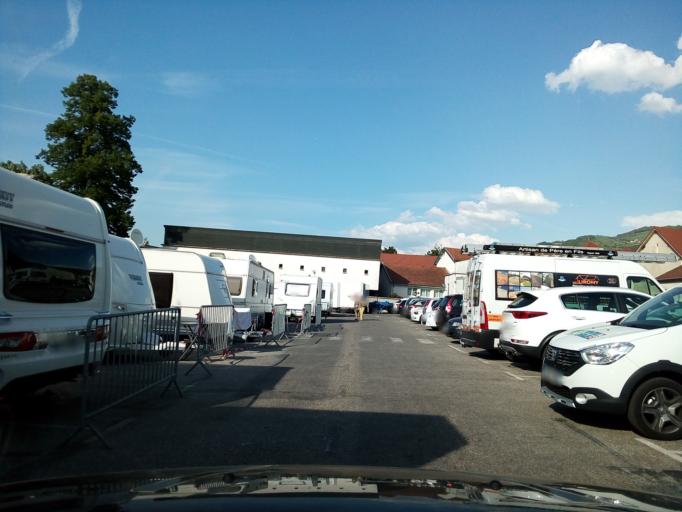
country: FR
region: Rhone-Alpes
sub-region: Departement de l'Isere
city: Domene
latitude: 45.2027
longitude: 5.8385
